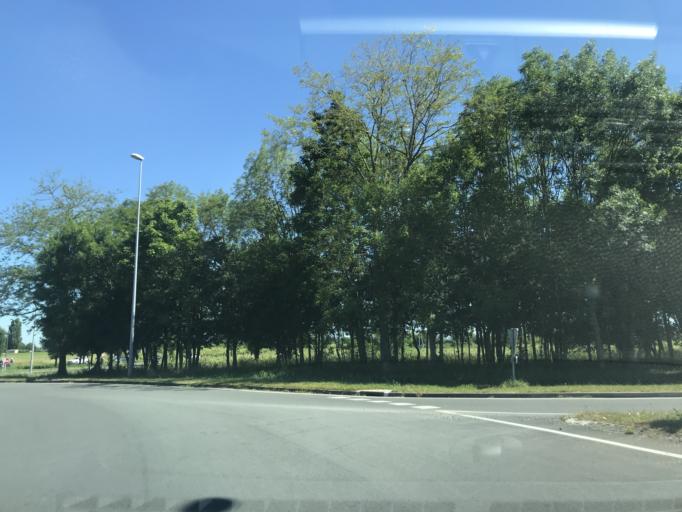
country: FR
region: Poitou-Charentes
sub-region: Departement de la Charente-Maritime
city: Cozes
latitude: 45.5776
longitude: -0.8237
